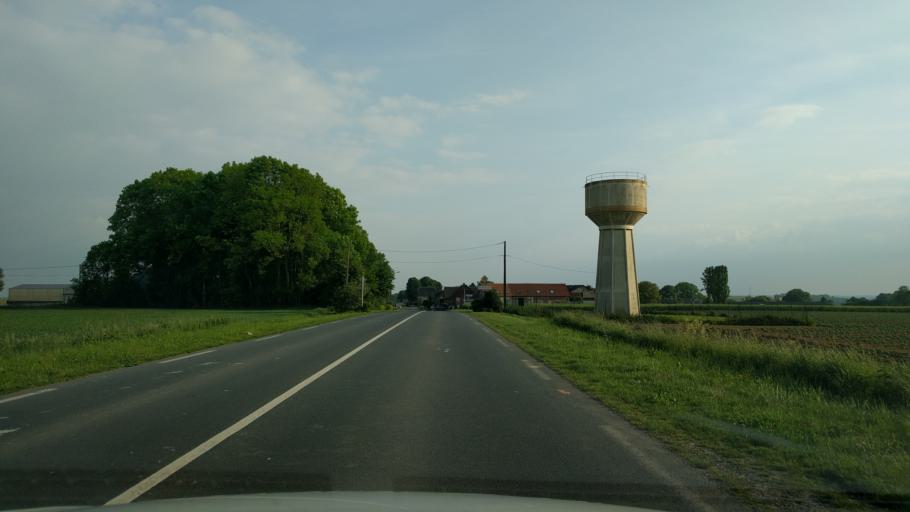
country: FR
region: Picardie
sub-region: Departement de la Somme
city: Moislains
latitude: 50.0097
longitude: 2.9114
